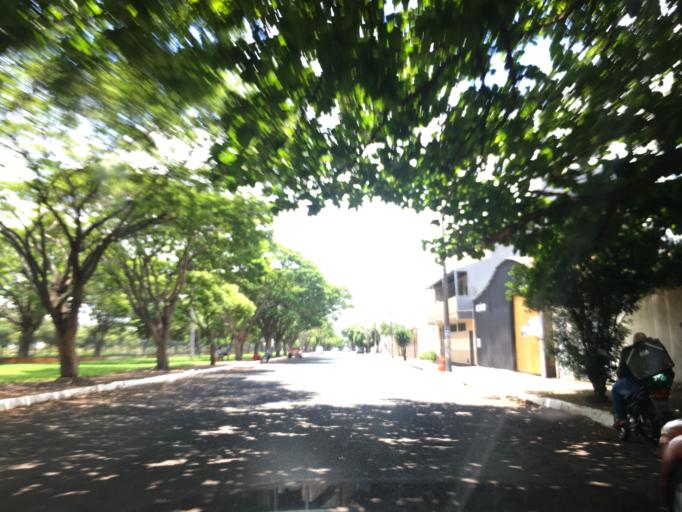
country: BR
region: Minas Gerais
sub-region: Uberlandia
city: Uberlandia
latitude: -18.9349
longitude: -48.3067
